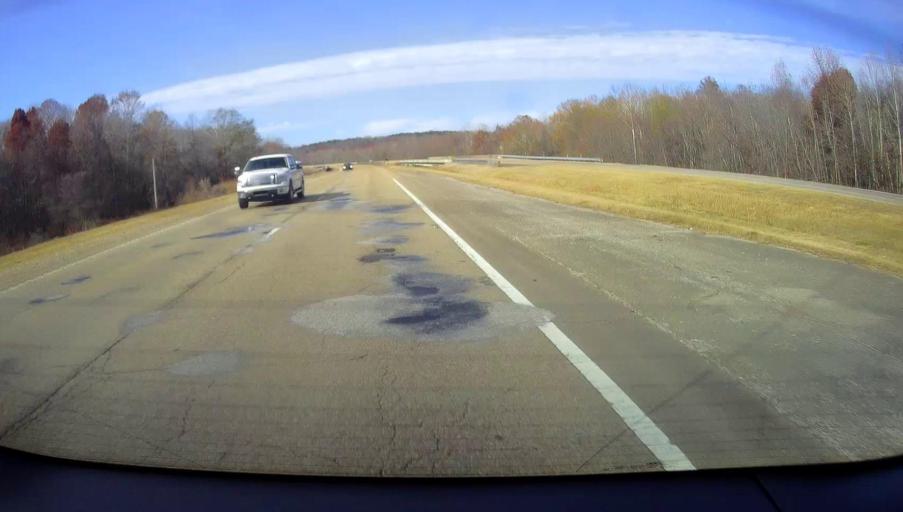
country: US
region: Mississippi
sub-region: Alcorn County
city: Corinth
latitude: 34.9427
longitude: -88.7840
